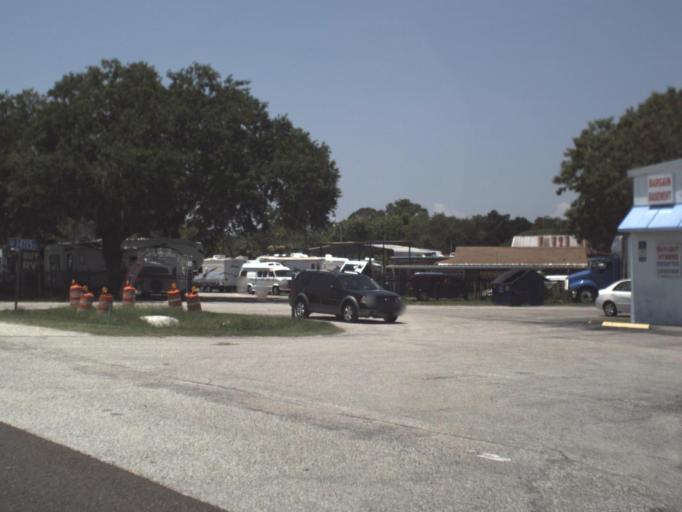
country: US
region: Florida
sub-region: Pasco County
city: Hudson
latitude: 28.3625
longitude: -82.6949
